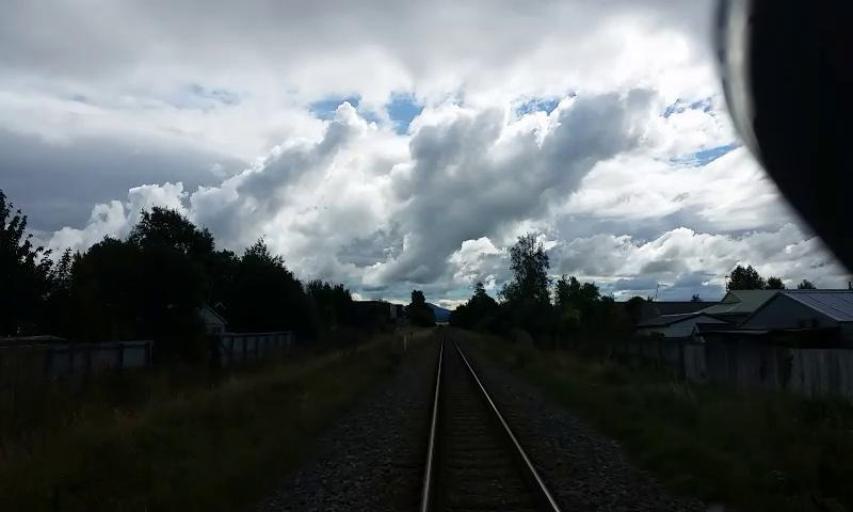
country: NZ
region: Canterbury
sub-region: Waimakariri District
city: Woodend
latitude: -43.3092
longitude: 172.5998
